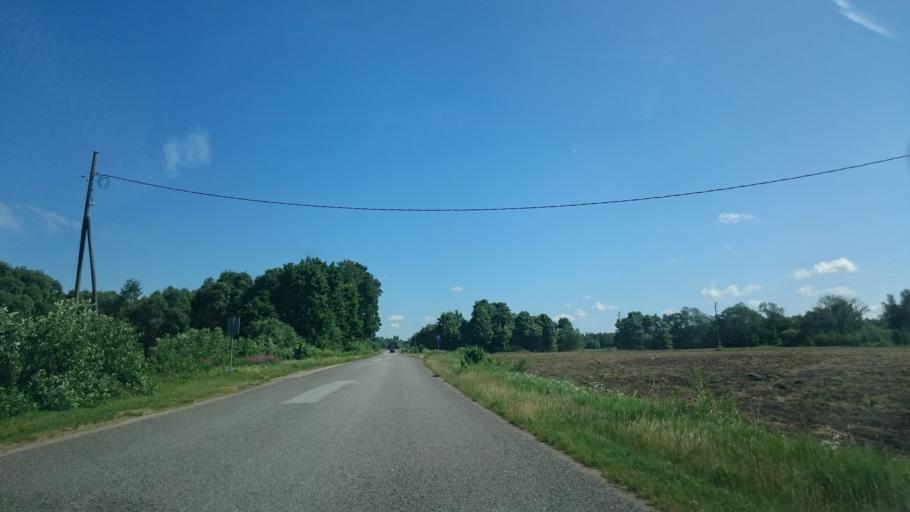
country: LV
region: Ludzas Rajons
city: Ludza
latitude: 56.5151
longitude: 27.7993
